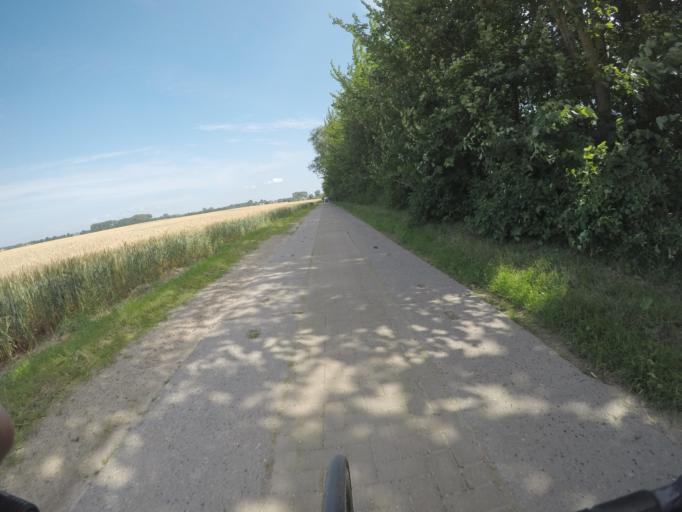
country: DE
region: Mecklenburg-Vorpommern
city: Rambin
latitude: 54.3609
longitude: 13.1803
